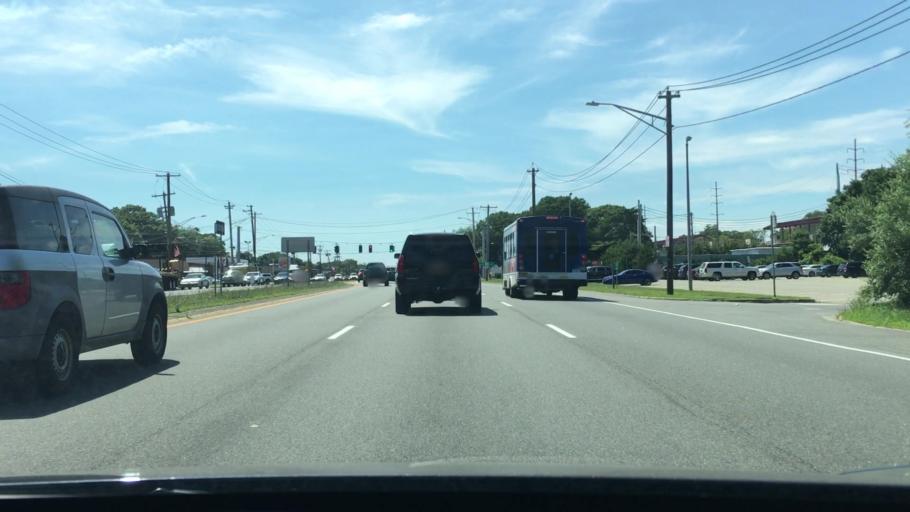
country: US
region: New York
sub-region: Nassau County
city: Massapequa
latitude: 40.6752
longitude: -73.4830
